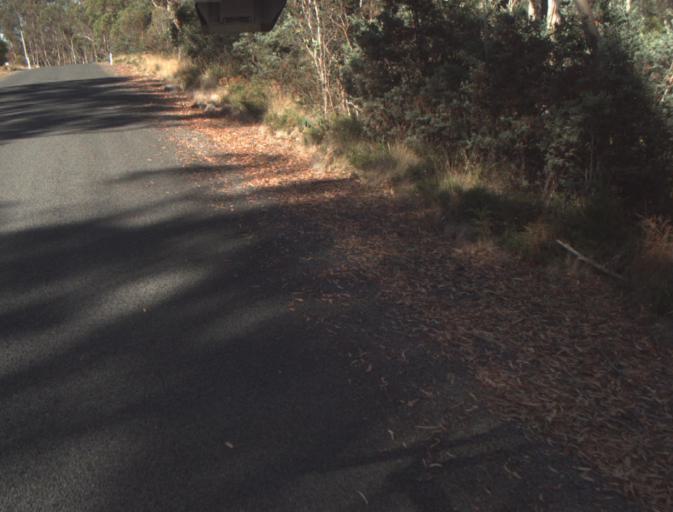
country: AU
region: Tasmania
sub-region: Launceston
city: Newstead
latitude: -41.3698
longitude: 147.2996
